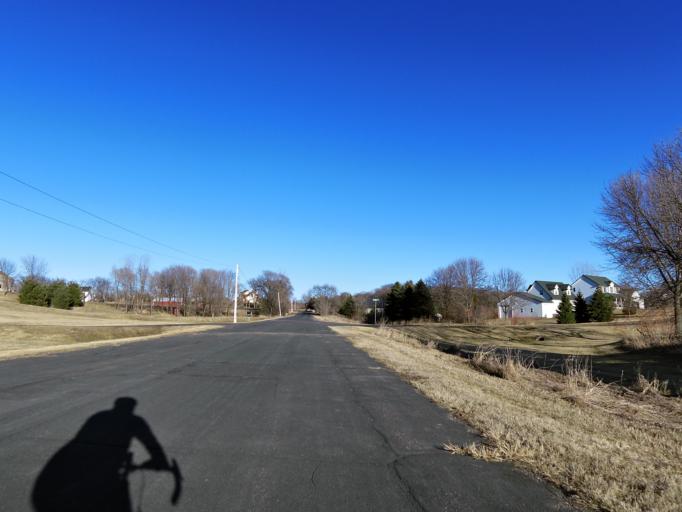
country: US
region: Minnesota
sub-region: Washington County
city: Lakeland
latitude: 44.9743
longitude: -92.8058
